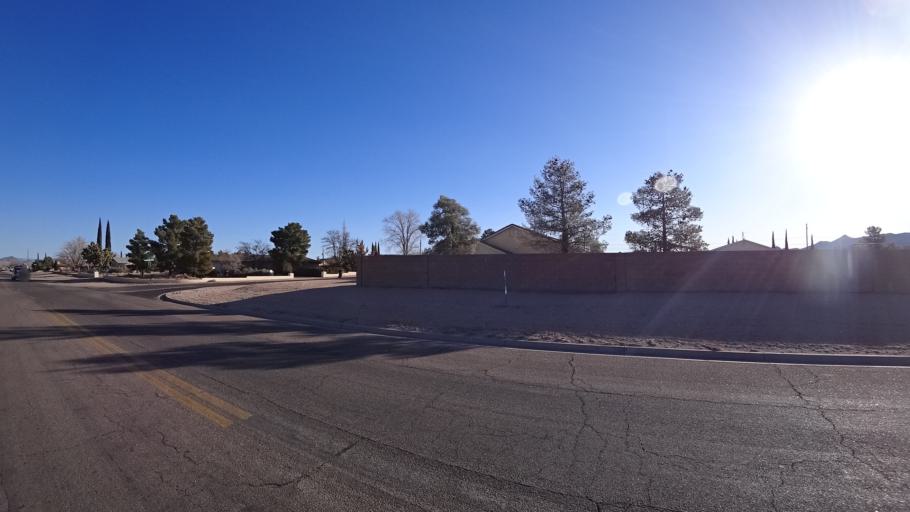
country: US
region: Arizona
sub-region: Mohave County
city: Kingman
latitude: 35.2028
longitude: -114.0114
